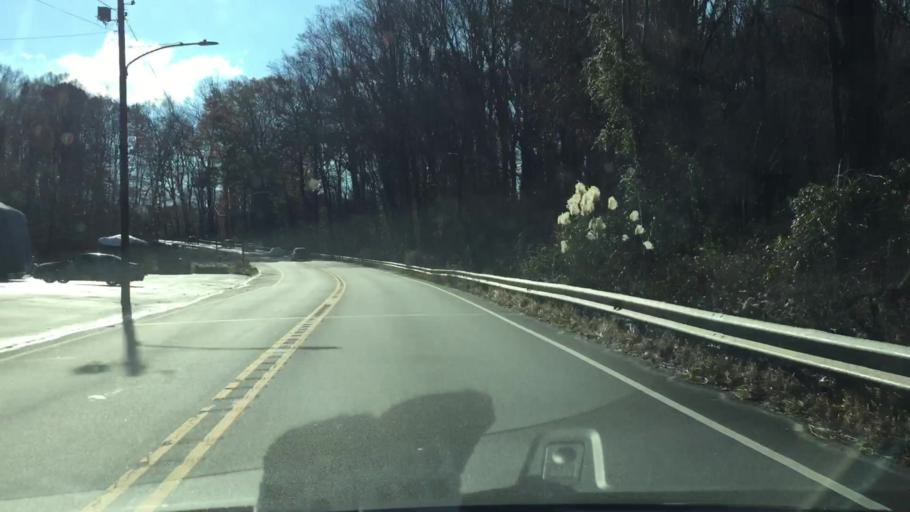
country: US
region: Pennsylvania
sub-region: Delaware County
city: Village Green-Green Ridge
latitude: 39.8794
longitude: -75.4295
